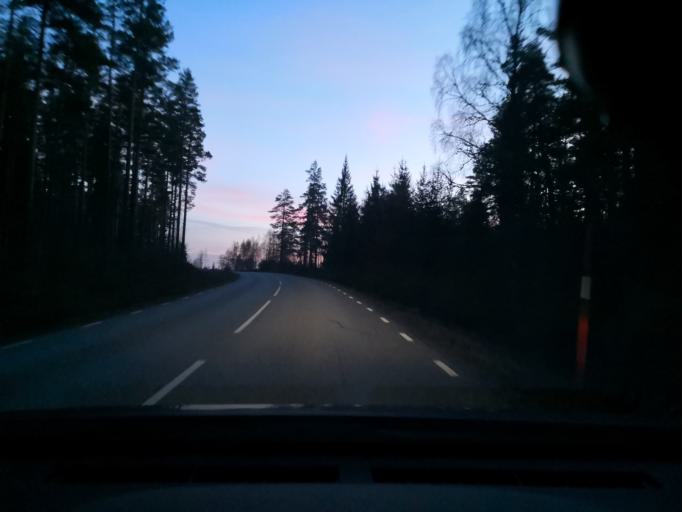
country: SE
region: OErebro
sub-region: Lindesbergs Kommun
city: Frovi
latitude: 59.3876
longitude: 15.4403
